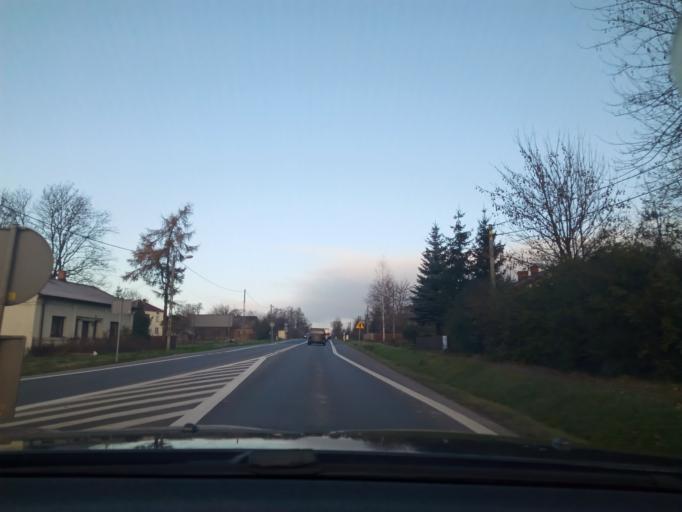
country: PL
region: Lesser Poland Voivodeship
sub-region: Powiat krakowski
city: Slomniki
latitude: 50.2833
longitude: 20.0559
